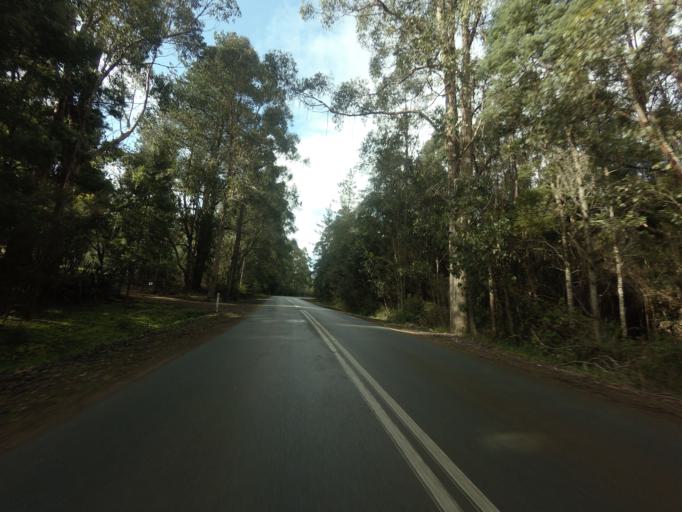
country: AU
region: Tasmania
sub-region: Huon Valley
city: Geeveston
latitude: -43.3528
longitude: 146.9569
